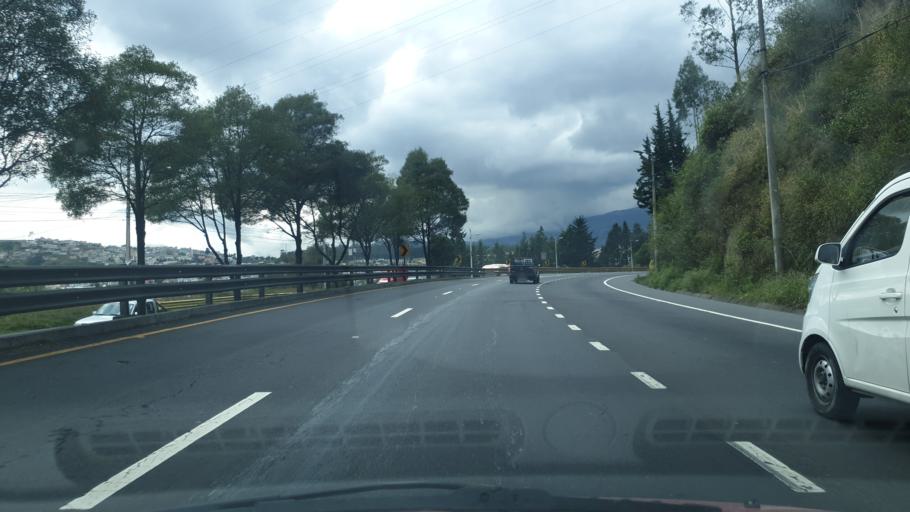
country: EC
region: Pichincha
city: Quito
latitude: -0.2469
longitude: -78.4807
